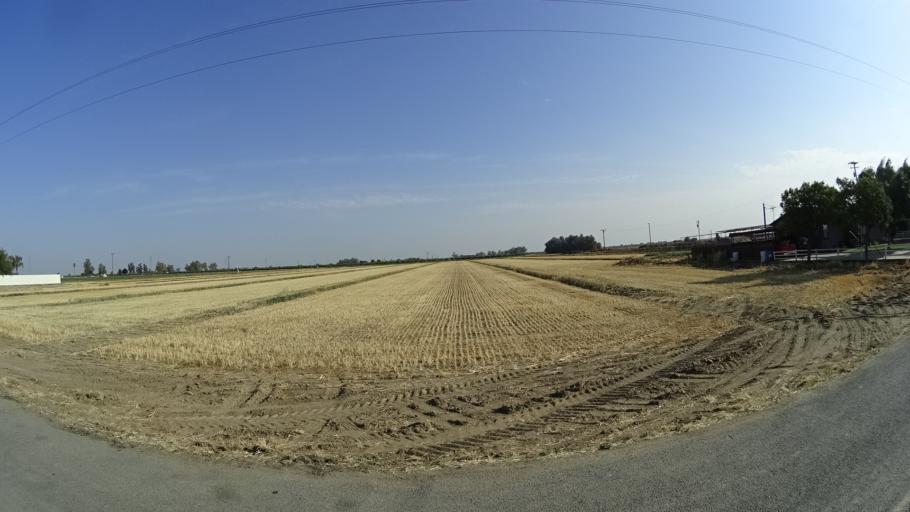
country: US
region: California
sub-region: Fresno County
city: Riverdale
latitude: 36.3583
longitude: -119.8815
